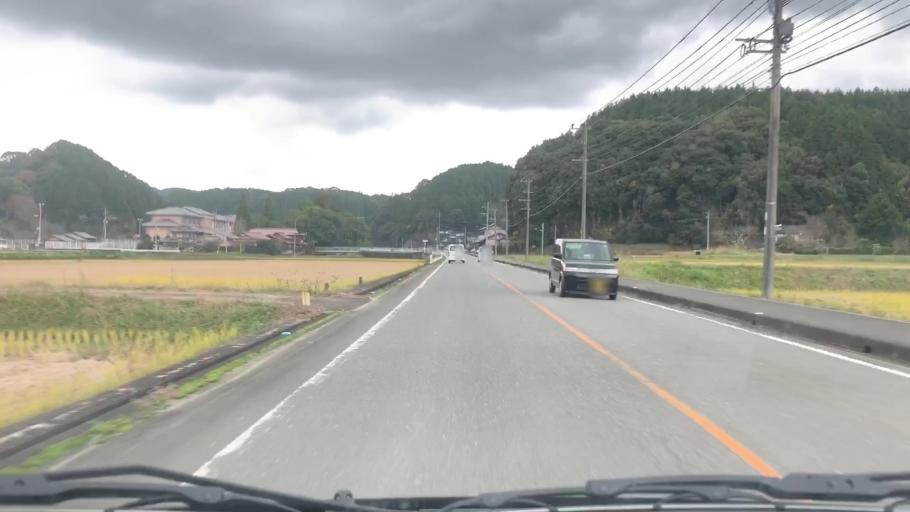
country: JP
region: Saga Prefecture
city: Ureshinomachi-shimojuku
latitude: 33.1377
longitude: 129.9741
